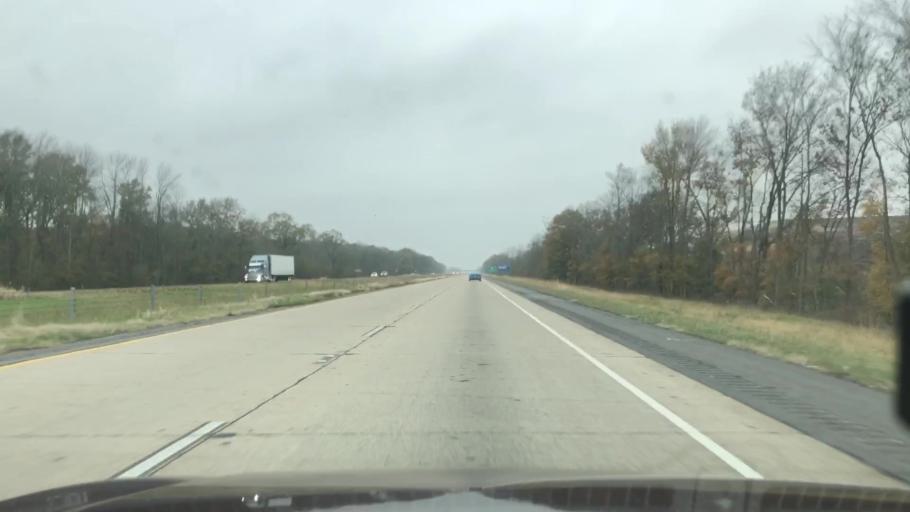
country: US
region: Louisiana
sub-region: Ouachita Parish
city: Lakeshore
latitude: 32.4875
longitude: -91.9716
